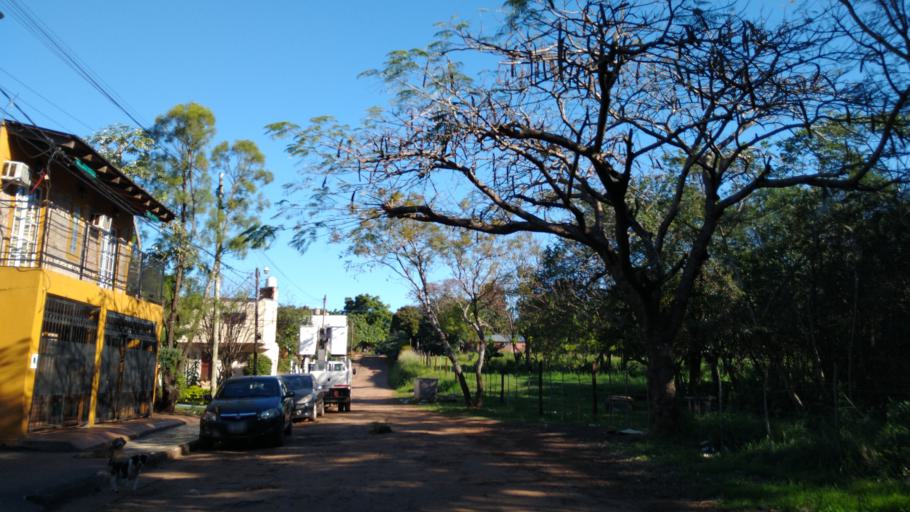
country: AR
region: Misiones
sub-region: Departamento de Capital
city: Posadas
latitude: -27.3628
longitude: -55.9292
